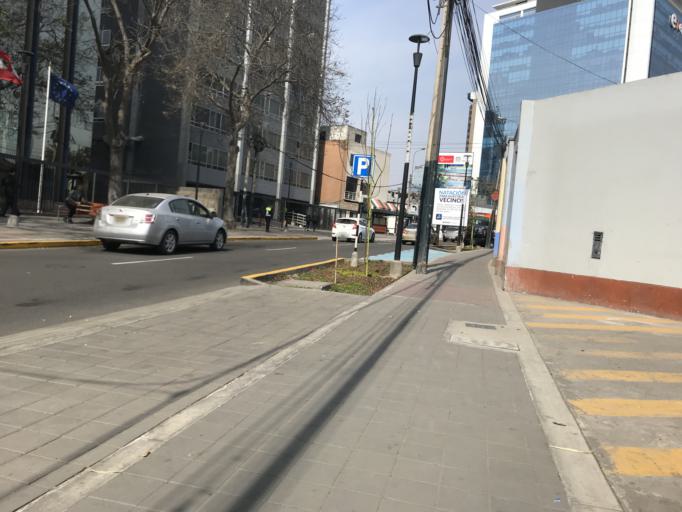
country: PE
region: Lima
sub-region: Lima
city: San Isidro
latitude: -12.0983
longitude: -77.0281
